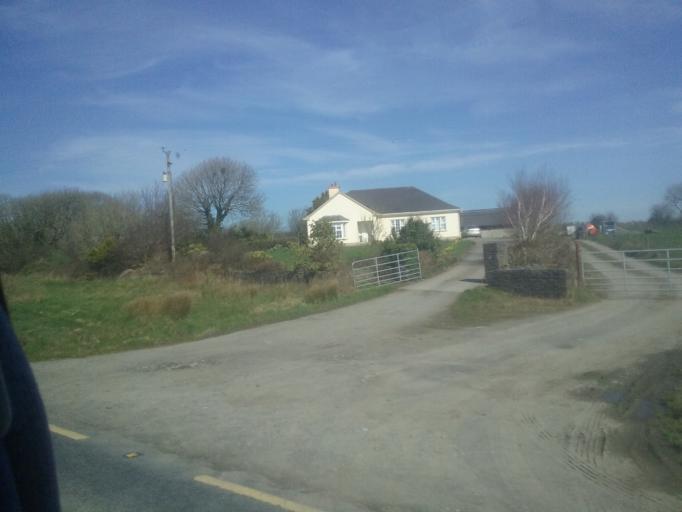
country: IE
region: Munster
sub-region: An Clar
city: Kilrush
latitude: 52.6151
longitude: -9.4524
